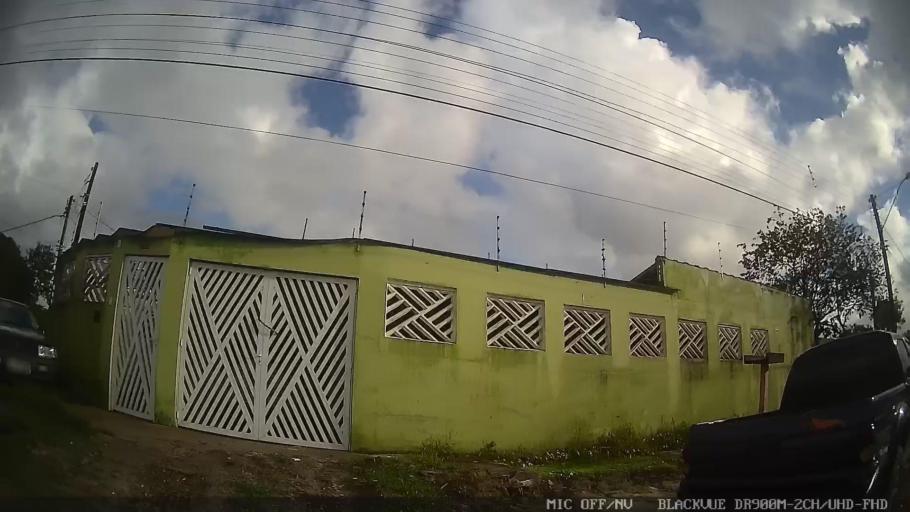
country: BR
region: Sao Paulo
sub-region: Itanhaem
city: Itanhaem
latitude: -24.1753
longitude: -46.8503
